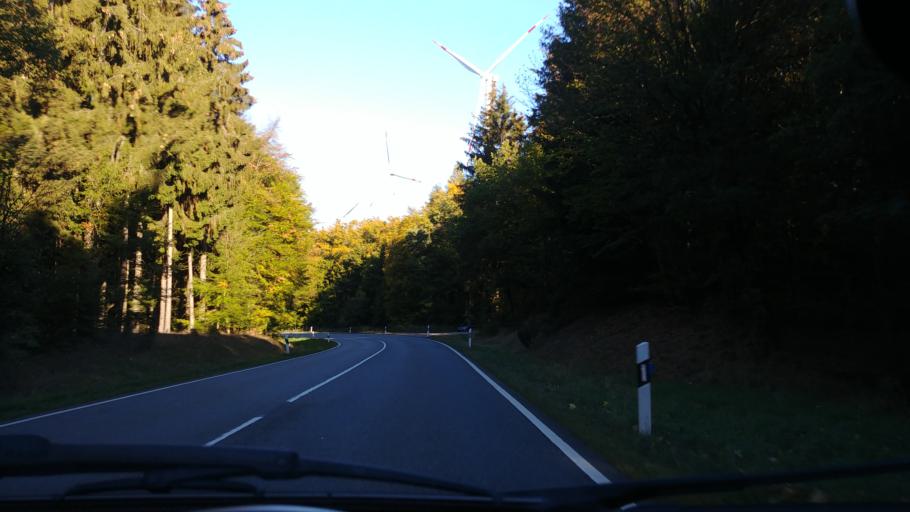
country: DE
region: Rheinland-Pfalz
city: Rettert
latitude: 50.1992
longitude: 7.9603
